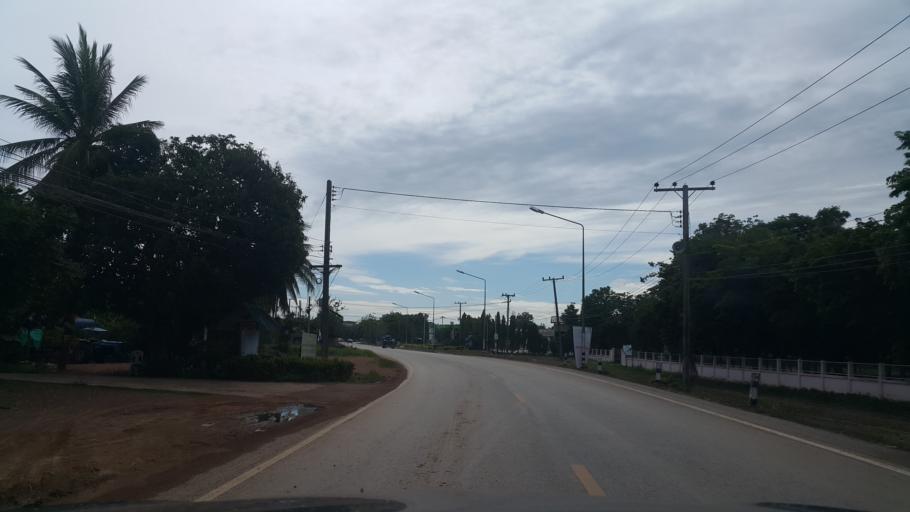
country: TH
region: Sukhothai
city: Si Nakhon
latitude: 17.2746
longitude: 99.9654
